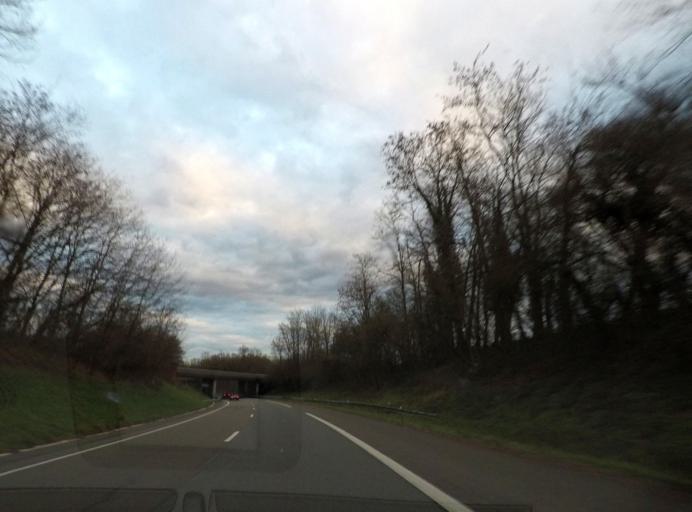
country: FR
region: Rhone-Alpes
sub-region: Departement de l'Ain
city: Saint-Martin-du-Mont
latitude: 46.0690
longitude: 5.3233
